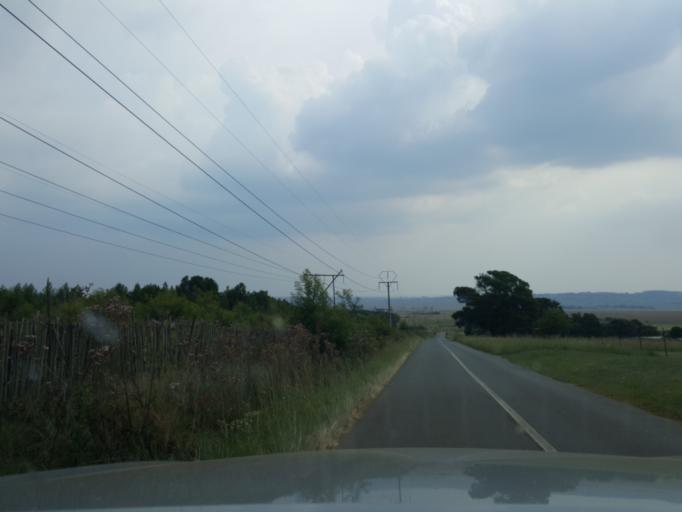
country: ZA
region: Gauteng
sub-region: City of Tshwane Metropolitan Municipality
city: Centurion
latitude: -25.8719
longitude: 28.3329
